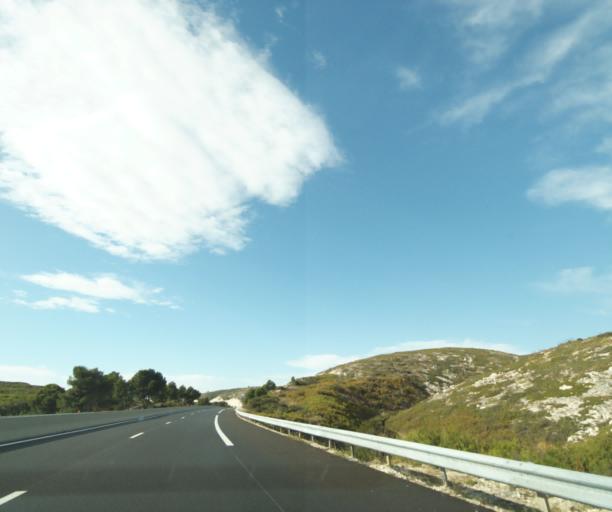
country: FR
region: Provence-Alpes-Cote d'Azur
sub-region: Departement des Bouches-du-Rhone
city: Carry-le-Rouet
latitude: 43.3397
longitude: 5.1369
